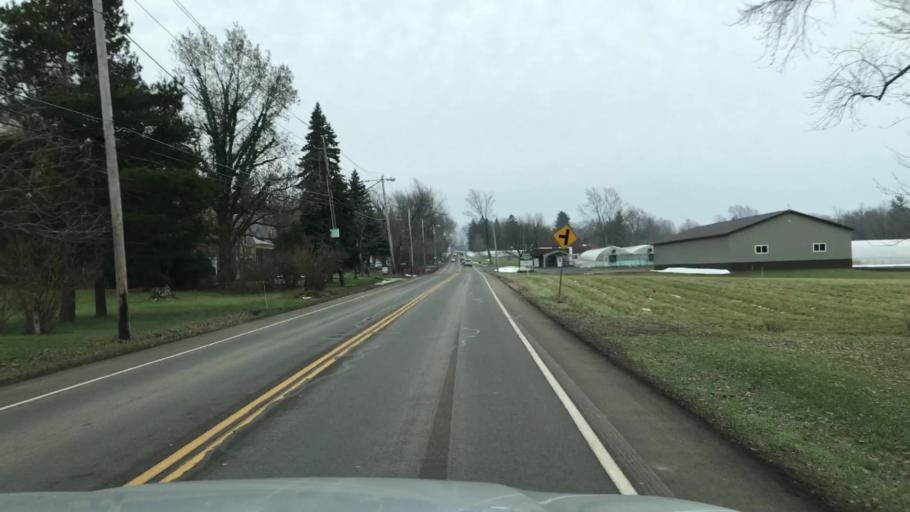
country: US
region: New York
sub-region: Erie County
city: Hamburg
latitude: 42.7455
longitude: -78.8049
